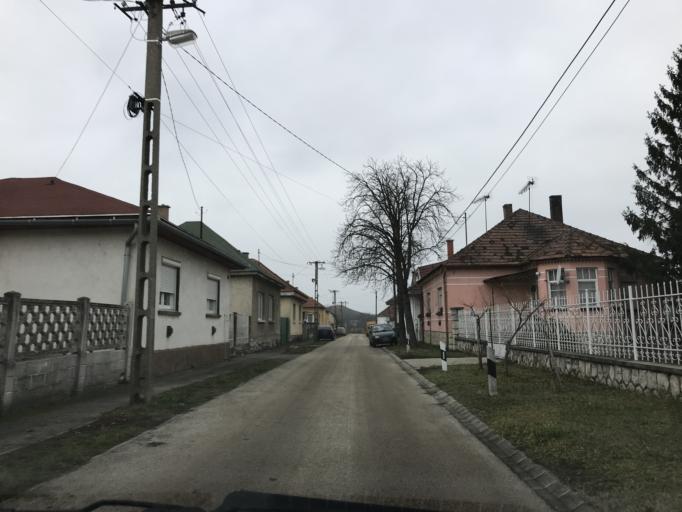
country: HU
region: Komarom-Esztergom
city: Tokod
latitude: 47.7279
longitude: 18.6632
